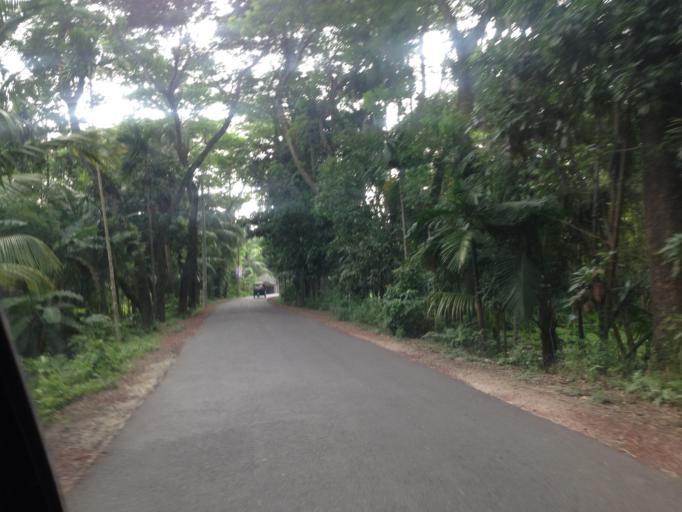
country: BD
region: Chittagong
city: Raipur
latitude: 23.0352
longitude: 90.7454
